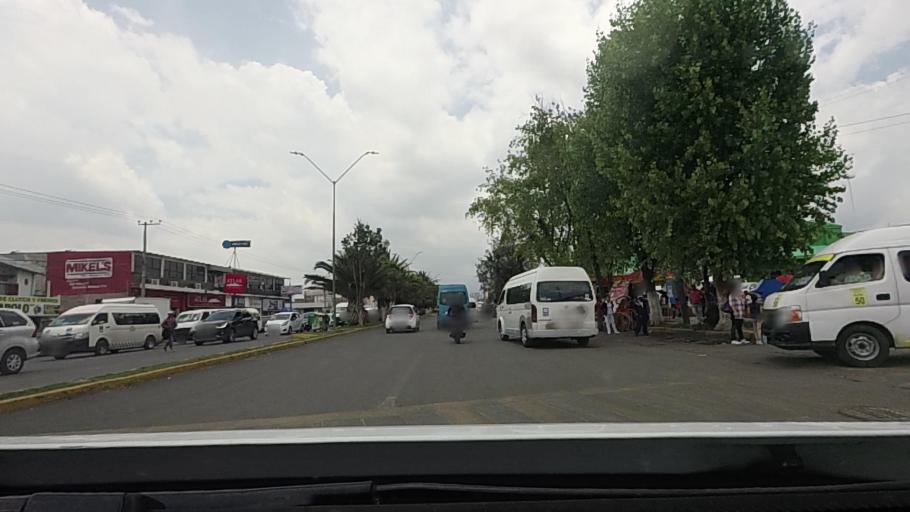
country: MX
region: Mexico
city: Chalco de Diaz Covarrubias
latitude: 19.2679
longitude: -98.8949
